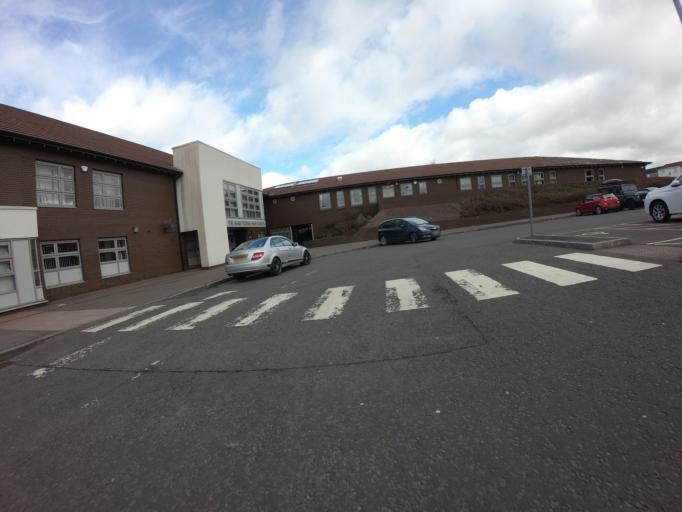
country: GB
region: Scotland
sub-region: West Lothian
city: Livingston
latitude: 55.8795
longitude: -3.5156
